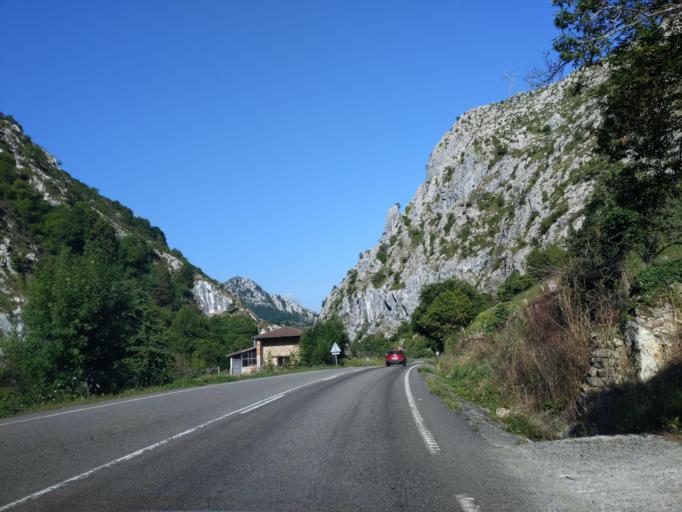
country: ES
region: Asturias
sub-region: Province of Asturias
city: Pola de Laviana
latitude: 43.2323
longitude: -5.4816
